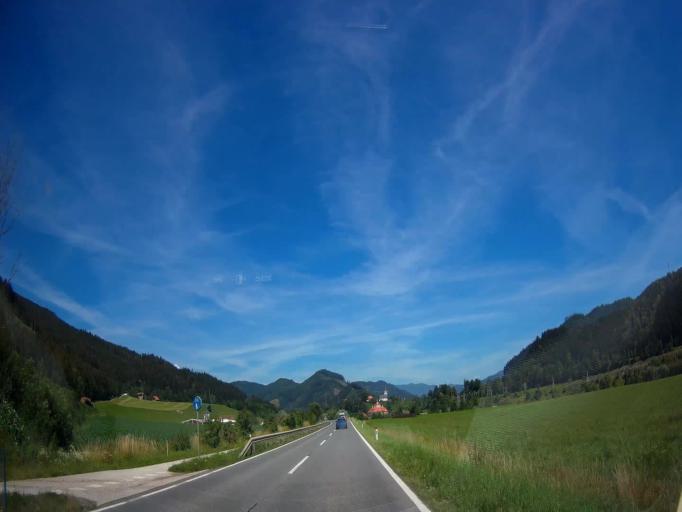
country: AT
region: Carinthia
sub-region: Politischer Bezirk Sankt Veit an der Glan
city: Althofen
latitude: 46.8838
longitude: 14.4448
